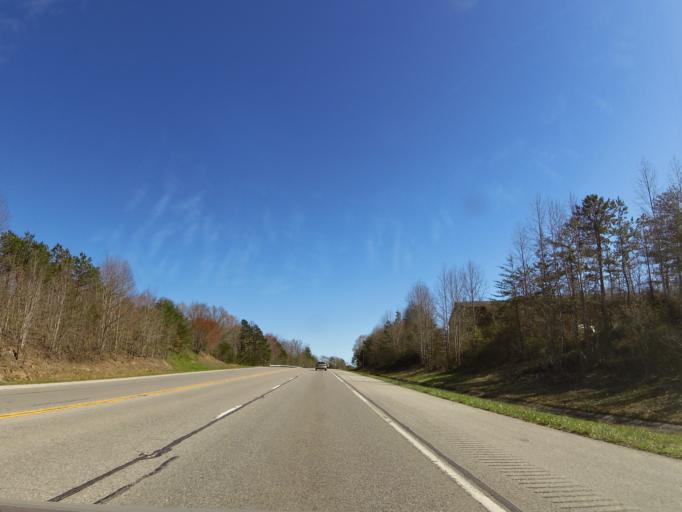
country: US
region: Kentucky
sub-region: McCreary County
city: Pine Knot
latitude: 36.6761
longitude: -84.4457
